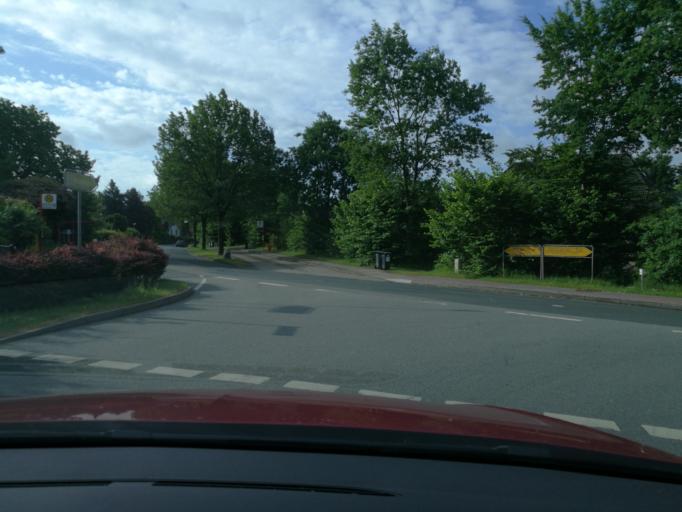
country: DE
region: Schleswig-Holstein
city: Hoisdorf
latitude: 53.6589
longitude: 10.3071
